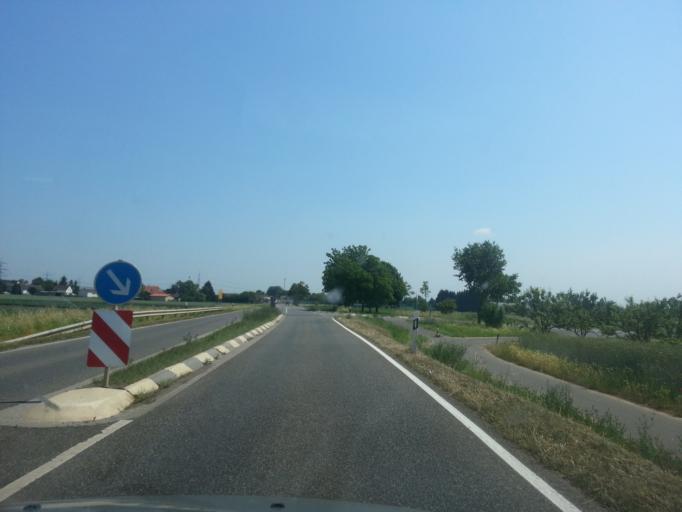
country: DE
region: Rheinland-Pfalz
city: Lambsheim
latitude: 49.5174
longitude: 8.2768
